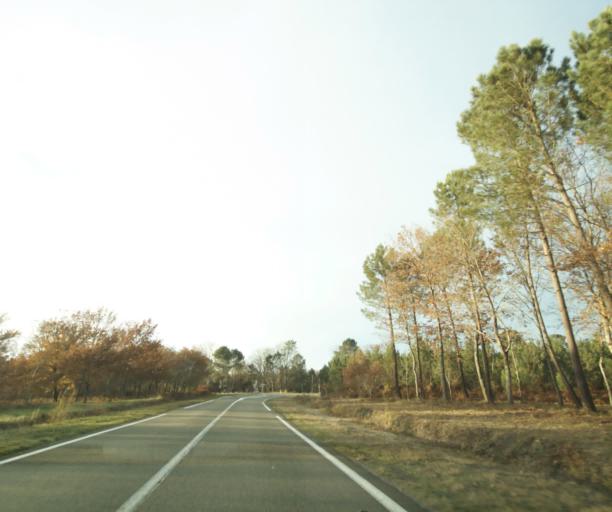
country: FR
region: Aquitaine
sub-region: Departement des Landes
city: Gabarret
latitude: 44.0676
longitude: -0.0589
